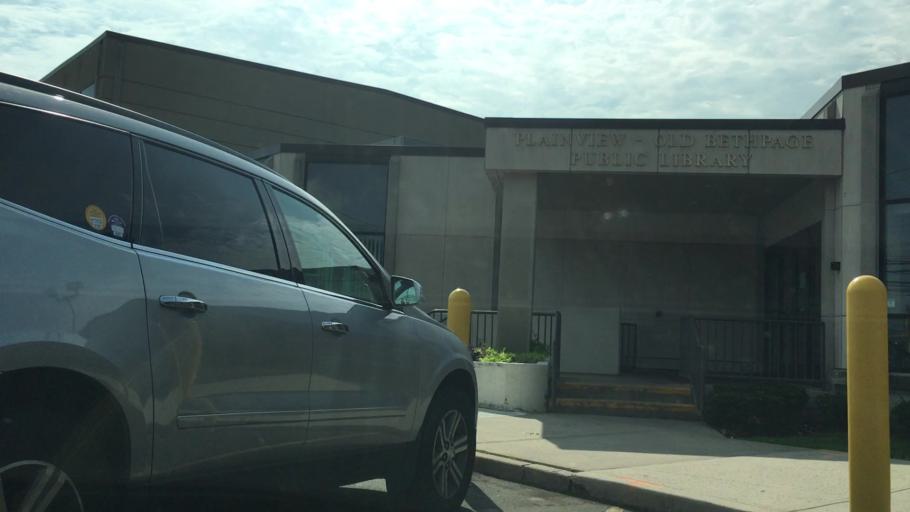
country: US
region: New York
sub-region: Nassau County
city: Plainview
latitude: 40.7752
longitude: -73.4734
